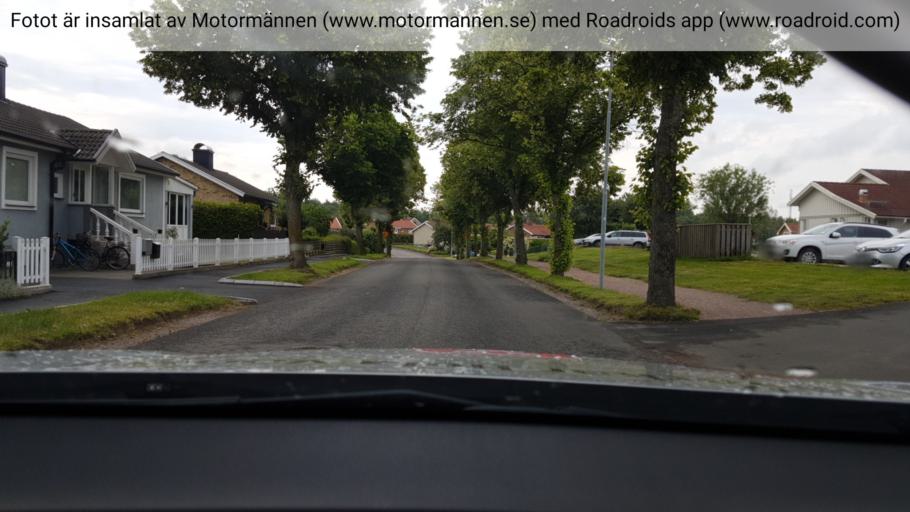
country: SE
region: Vaestra Goetaland
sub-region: Skovde Kommun
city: Skoevde
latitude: 58.3857
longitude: 13.8672
